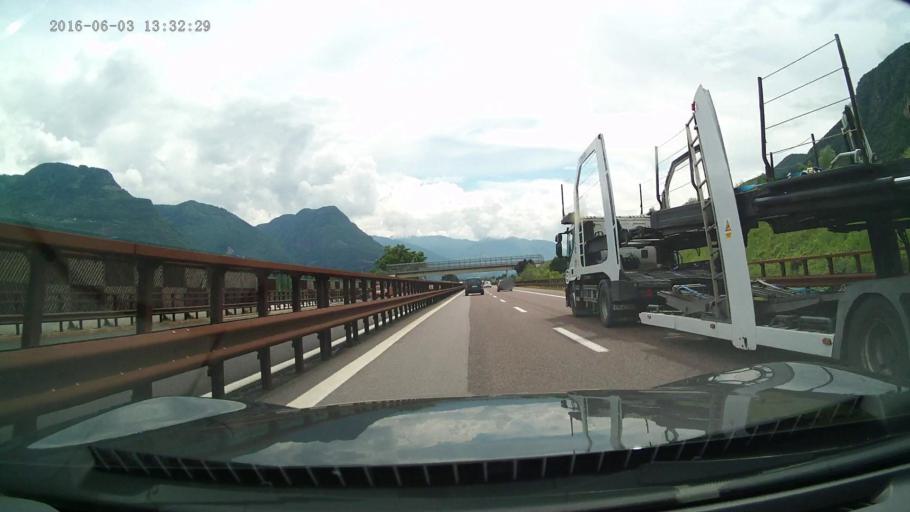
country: IT
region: Trentino-Alto Adige
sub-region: Bolzano
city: Laives
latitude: 46.4347
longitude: 11.3169
